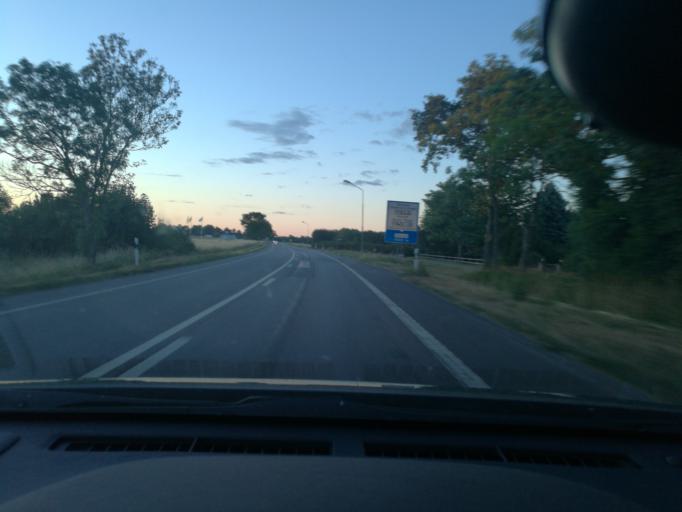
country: SE
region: Kalmar
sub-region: Borgholms Kommun
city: Borgholm
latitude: 56.7782
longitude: 16.5756
